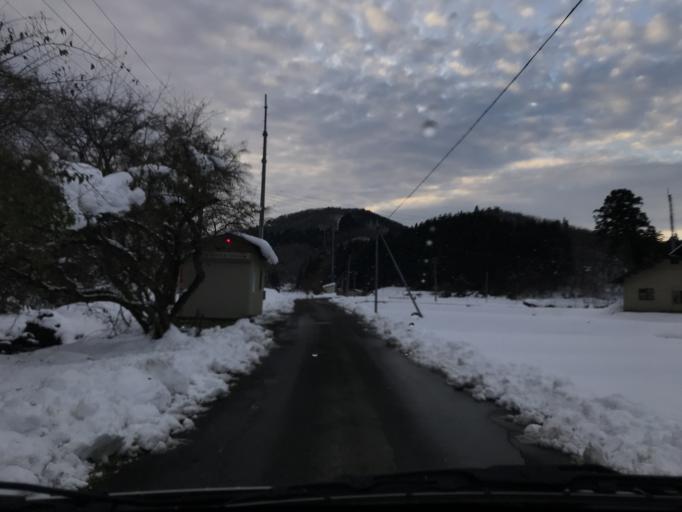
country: JP
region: Iwate
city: Mizusawa
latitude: 39.0470
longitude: 141.0162
